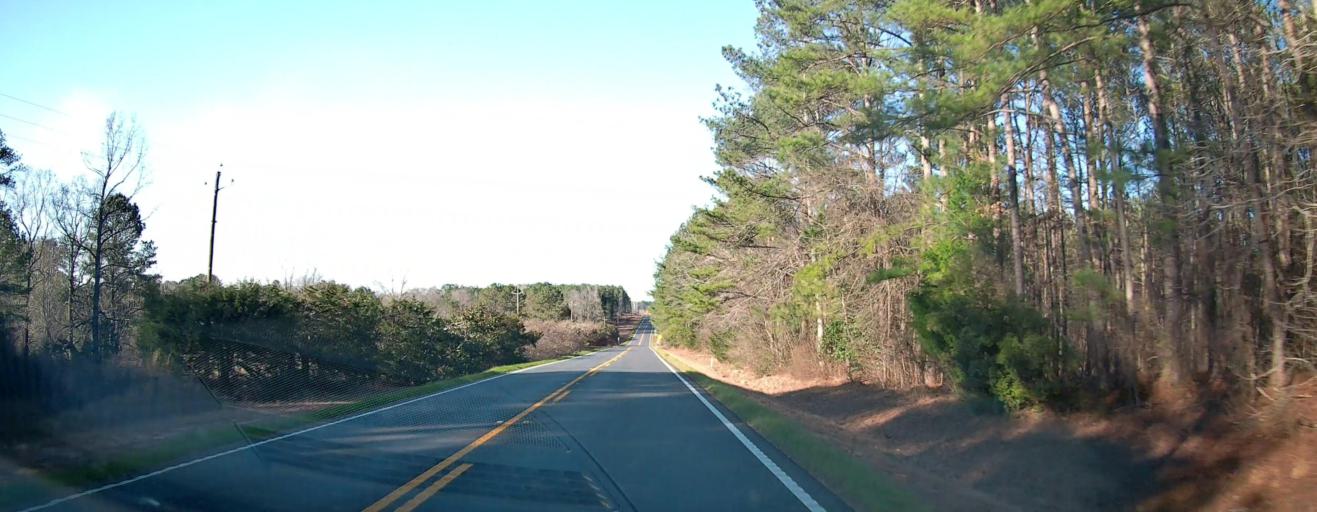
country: US
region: Georgia
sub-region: Talbot County
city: Sardis
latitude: 32.7851
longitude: -84.6927
